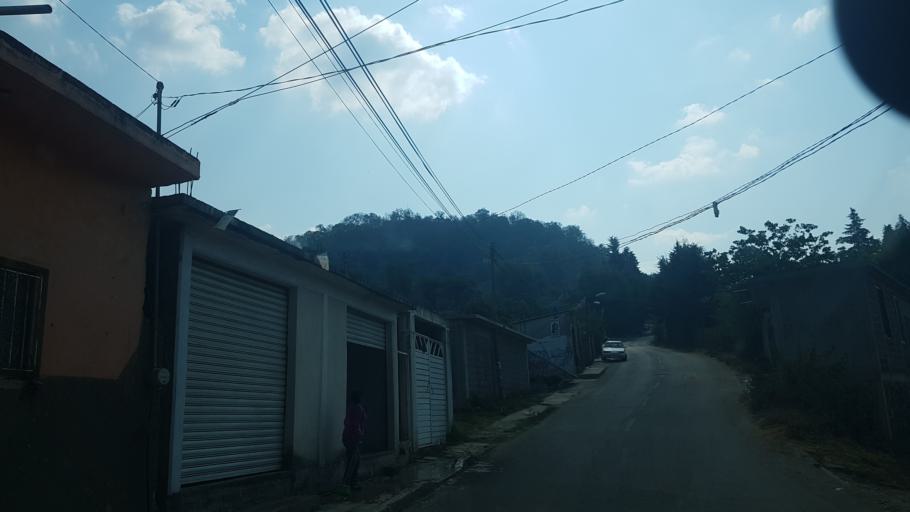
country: MX
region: Puebla
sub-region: Tochimilco
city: San Antonio Alpanocan
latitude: 18.8778
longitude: -98.7054
